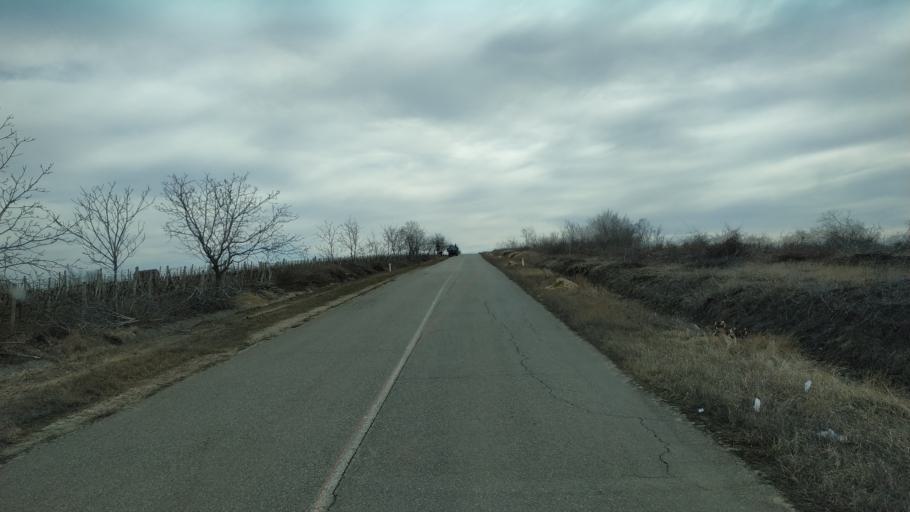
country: MD
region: Nisporeni
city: Nisporeni
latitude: 46.9556
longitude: 28.2359
